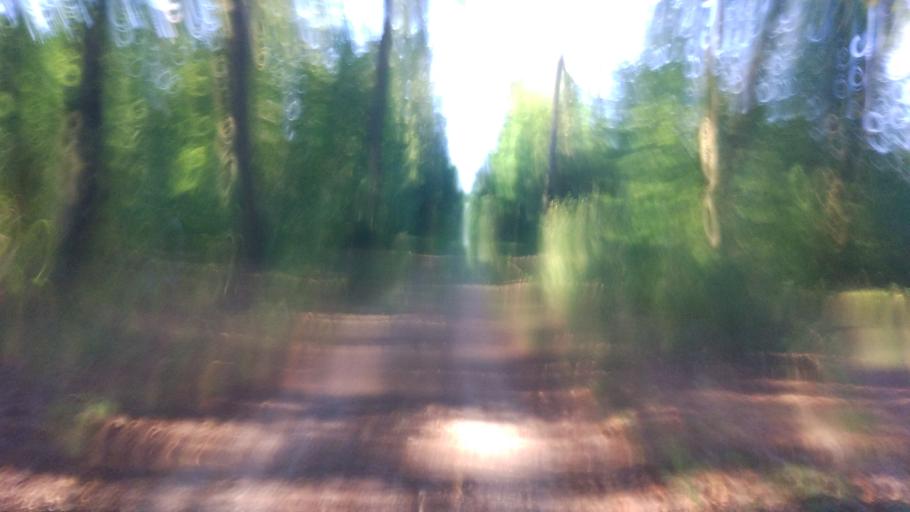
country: FR
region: Alsace
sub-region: Departement du Bas-Rhin
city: Gries
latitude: 48.7582
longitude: 7.8284
